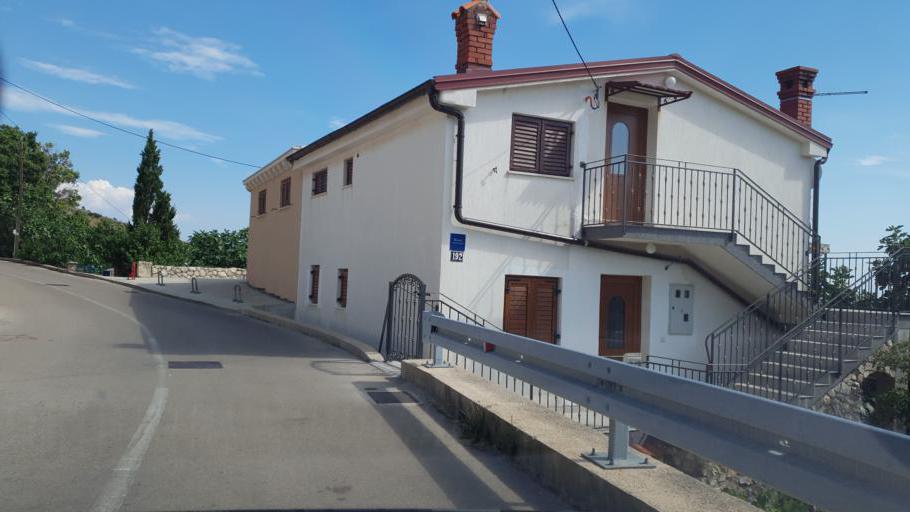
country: HR
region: Primorsko-Goranska
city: Punat
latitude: 44.9577
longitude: 14.6888
